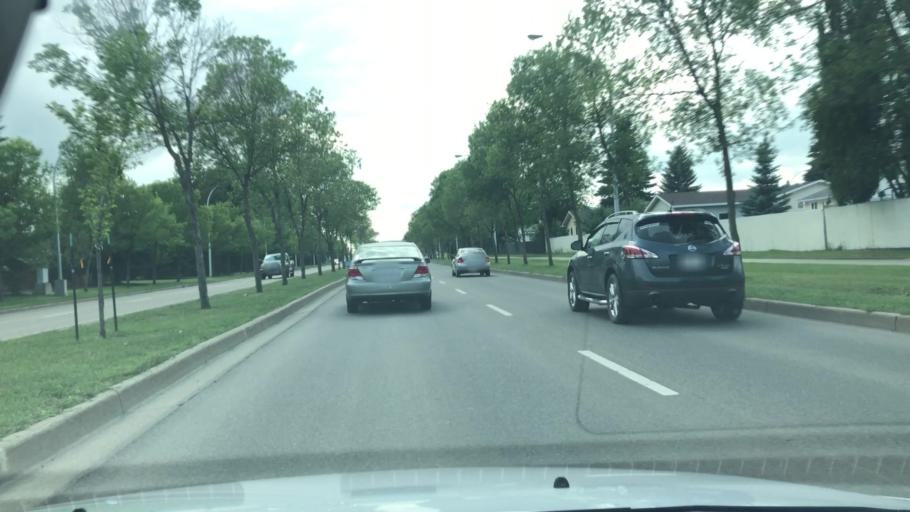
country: CA
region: Alberta
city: Edmonton
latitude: 53.6170
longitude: -113.5347
